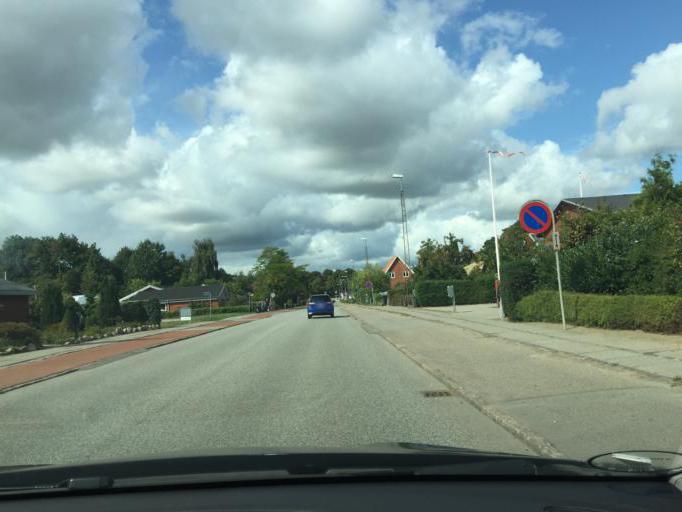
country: DK
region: Central Jutland
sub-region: Odder Kommune
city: Odder
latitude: 55.9775
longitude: 10.1571
